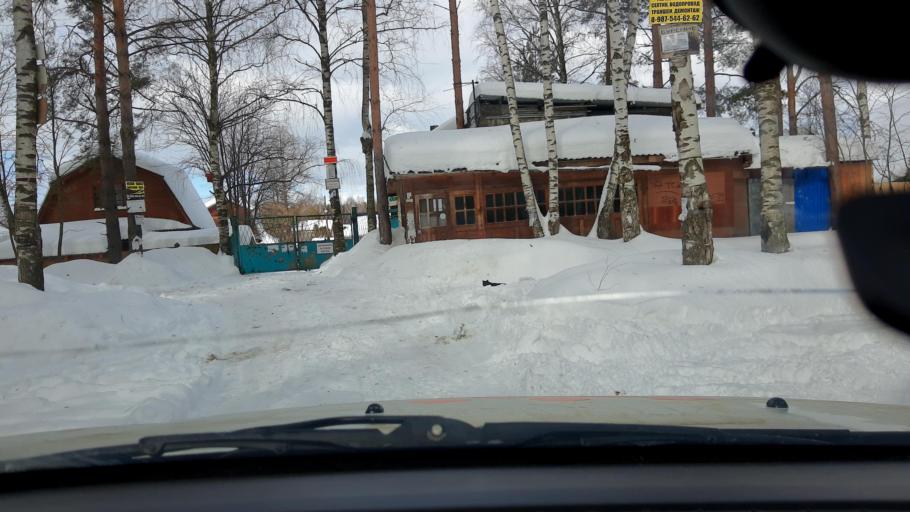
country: RU
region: Nizjnij Novgorod
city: Neklyudovo
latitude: 56.4497
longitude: 43.9812
